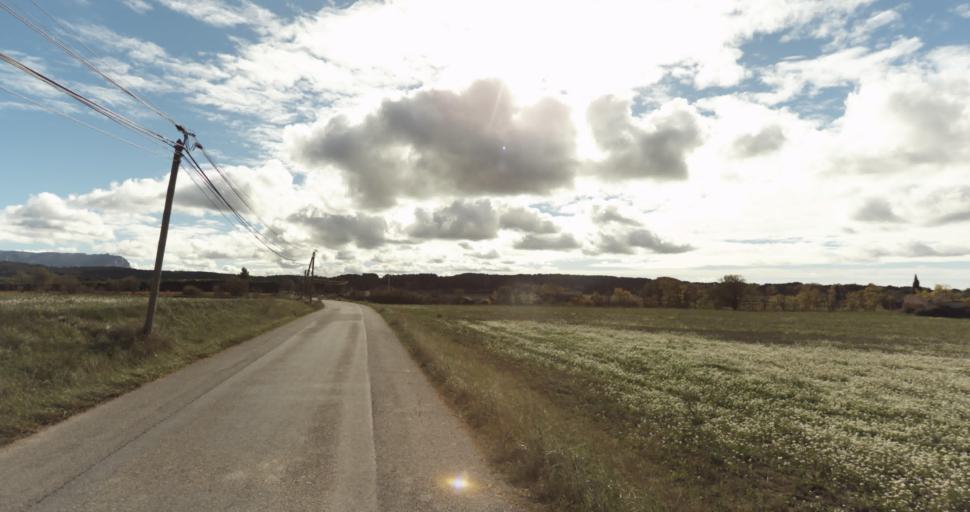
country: FR
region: Provence-Alpes-Cote d'Azur
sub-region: Departement des Bouches-du-Rhone
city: Venelles
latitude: 43.5878
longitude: 5.4883
